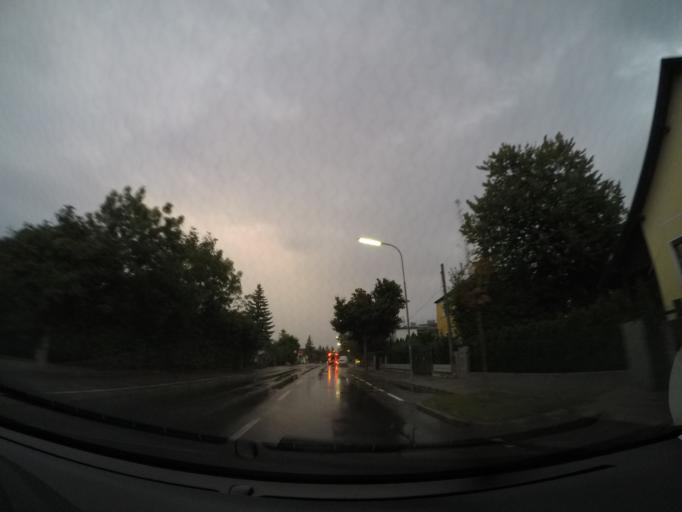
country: AT
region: Lower Austria
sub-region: Politischer Bezirk Baden
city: Bad Voslau
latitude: 47.9586
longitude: 16.2175
